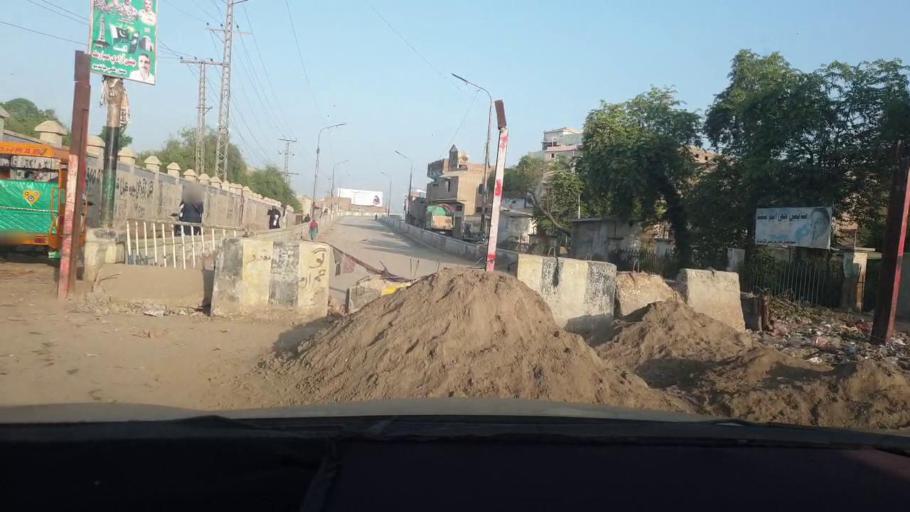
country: PK
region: Sindh
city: Larkana
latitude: 27.5432
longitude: 68.2119
